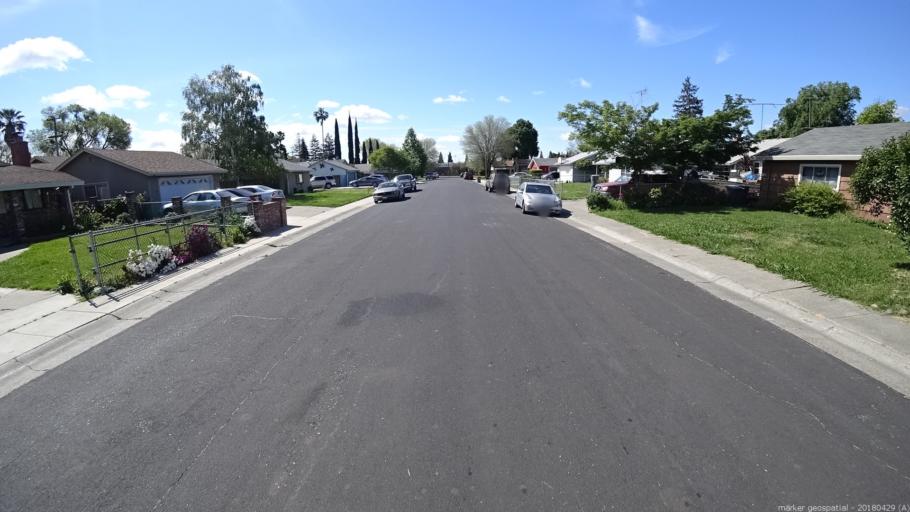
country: US
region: California
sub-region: Yolo County
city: West Sacramento
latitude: 38.5771
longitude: -121.5601
